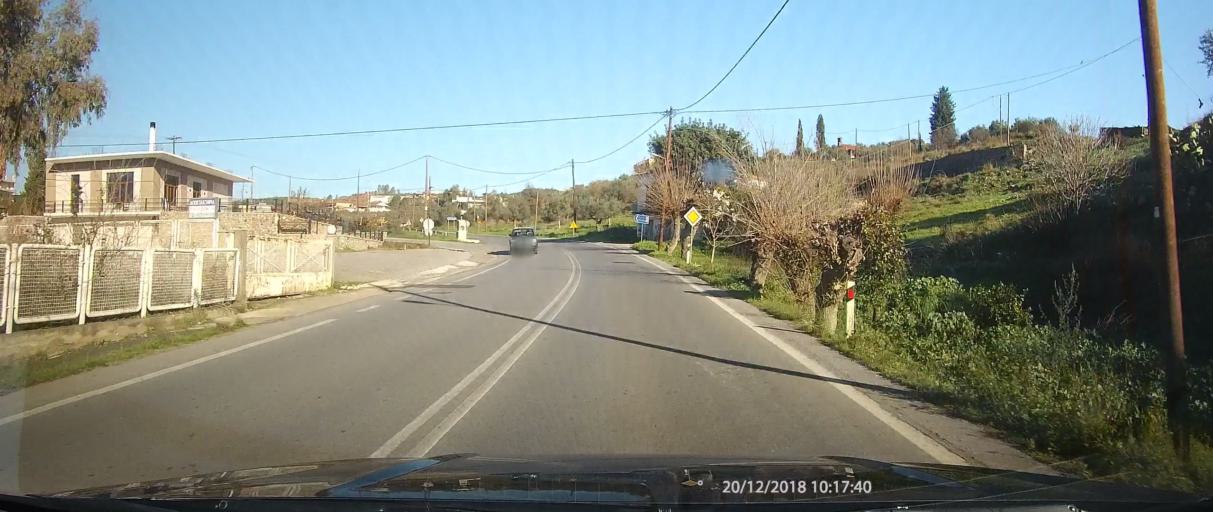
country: GR
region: Peloponnese
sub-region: Nomos Lakonias
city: Sparti
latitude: 37.1095
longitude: 22.4339
